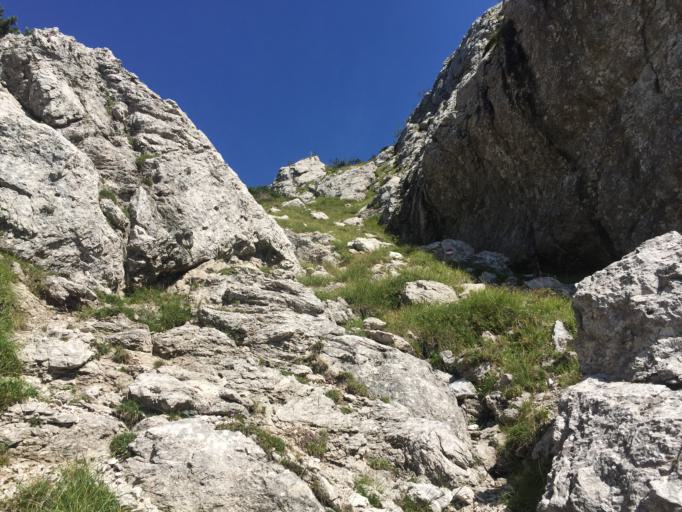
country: IT
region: Friuli Venezia Giulia
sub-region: Provincia di Pordenone
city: Tramonti di Sopra
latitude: 46.3199
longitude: 12.7296
